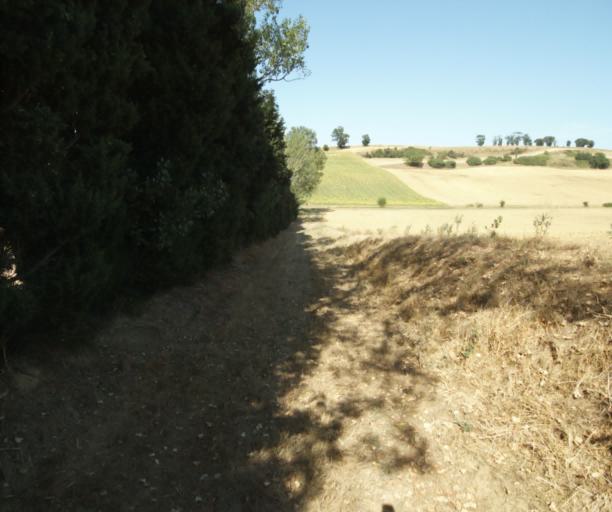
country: FR
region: Midi-Pyrenees
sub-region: Departement de la Haute-Garonne
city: Saint-Felix-Lauragais
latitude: 43.4345
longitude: 1.8485
